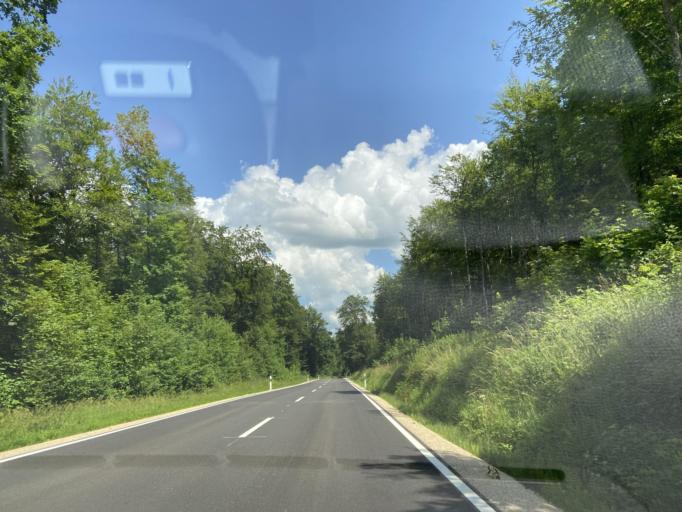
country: DE
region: Baden-Wuerttemberg
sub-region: Tuebingen Region
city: Veringenstadt
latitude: 48.1683
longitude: 9.1794
